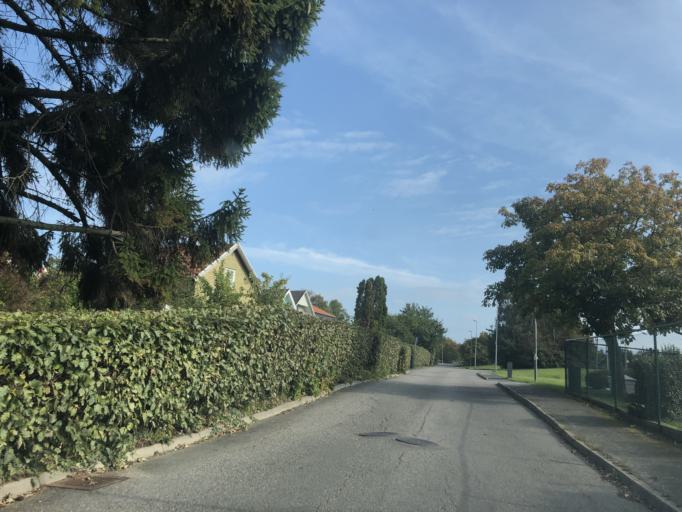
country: SE
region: Vaestra Goetaland
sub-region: Goteborg
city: Majorna
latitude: 57.6458
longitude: 11.8810
